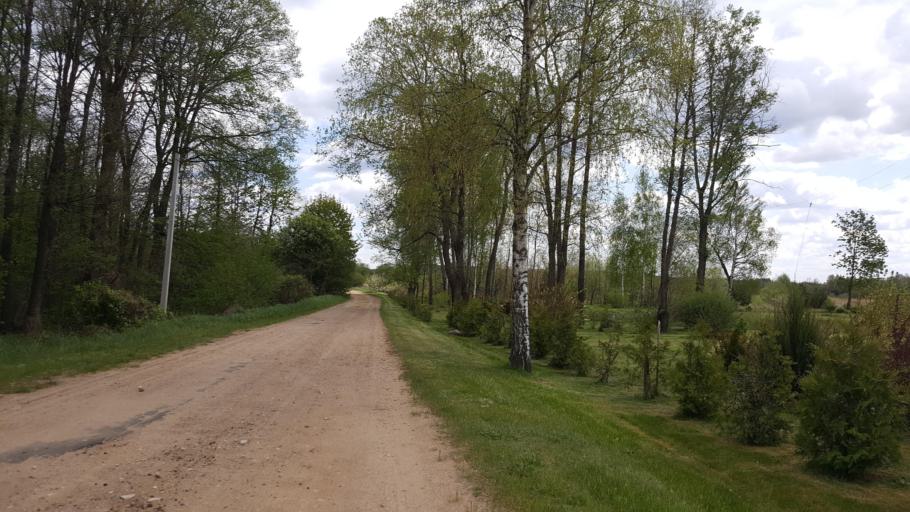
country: BY
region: Brest
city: Zhabinka
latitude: 52.3922
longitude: 24.0146
